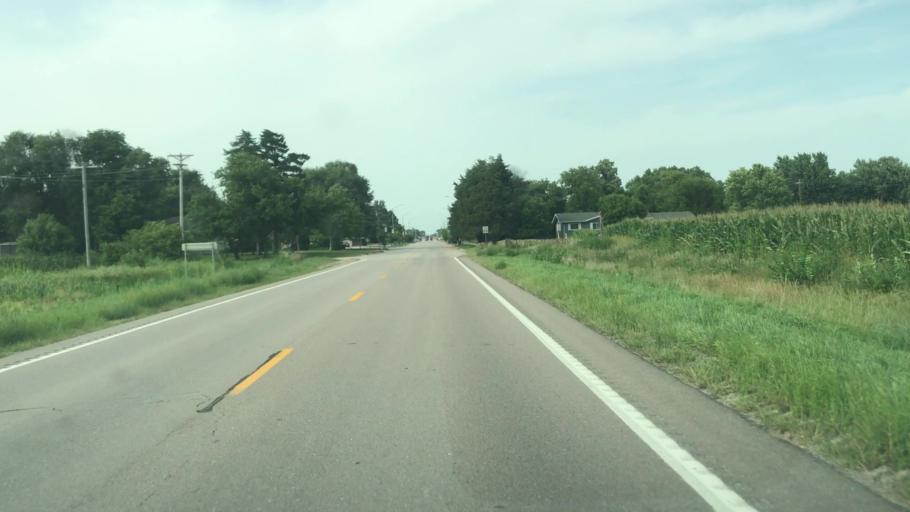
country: US
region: Nebraska
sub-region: Hall County
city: Wood River
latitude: 40.9953
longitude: -98.6075
